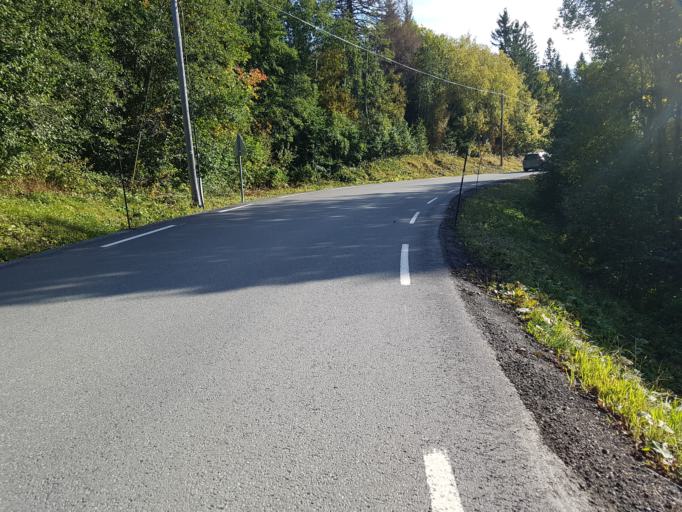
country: NO
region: Sor-Trondelag
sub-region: Malvik
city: Malvik
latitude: 63.3662
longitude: 10.6231
